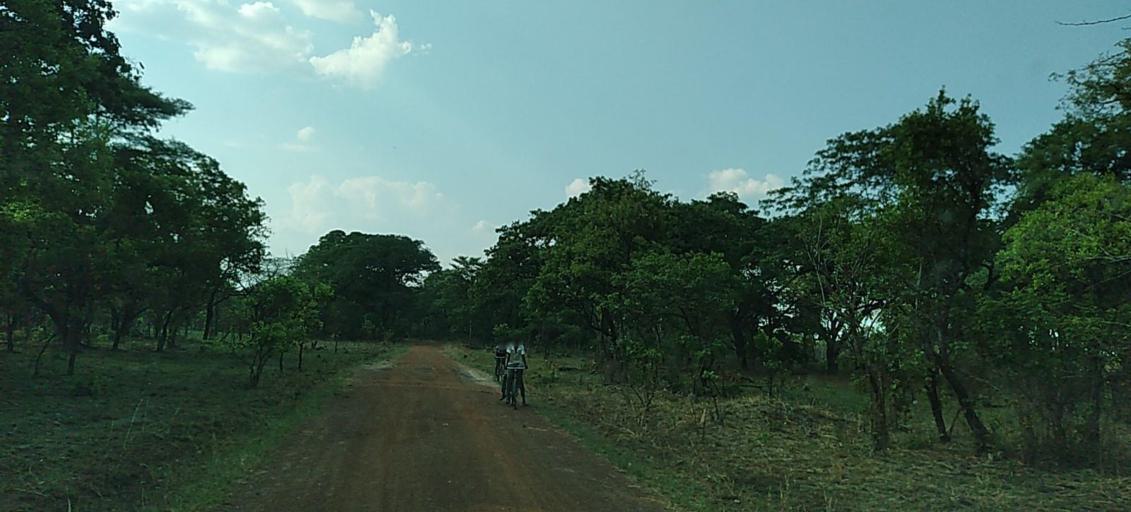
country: ZM
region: Copperbelt
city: Mpongwe
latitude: -13.4352
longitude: 28.0587
